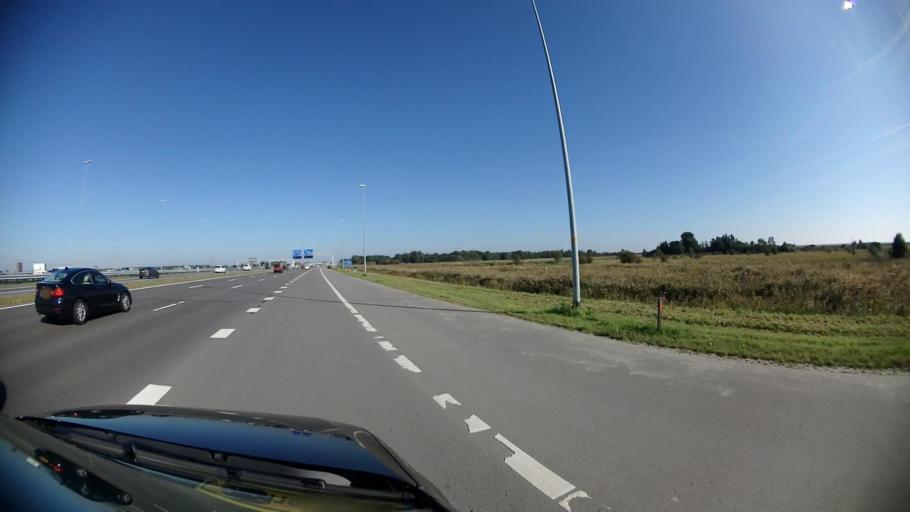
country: NL
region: North Holland
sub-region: Gemeente Naarden
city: Naarden
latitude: 52.3342
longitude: 5.1574
